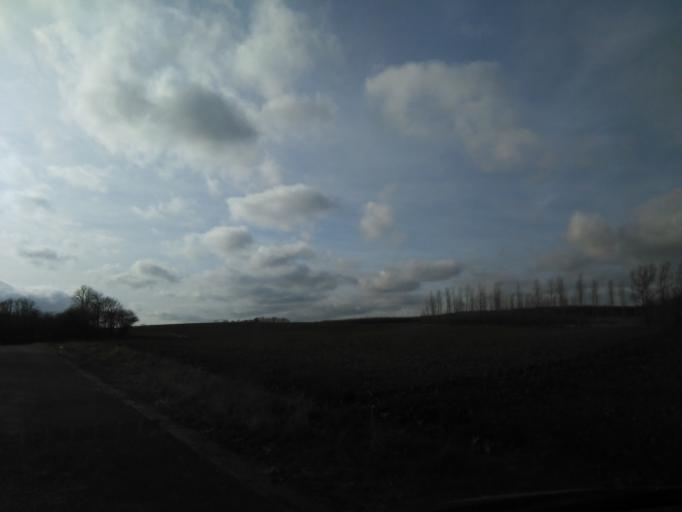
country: DK
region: Central Jutland
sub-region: Arhus Kommune
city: Stavtrup
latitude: 56.1649
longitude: 10.0760
